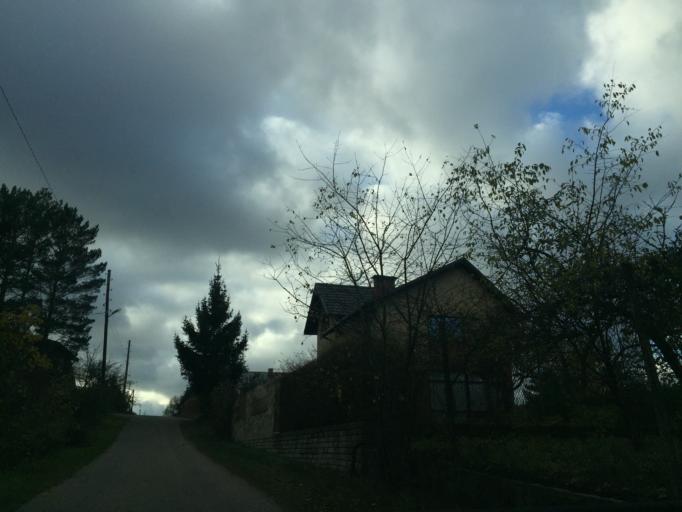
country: LV
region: Carnikava
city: Carnikava
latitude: 57.1516
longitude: 24.2887
